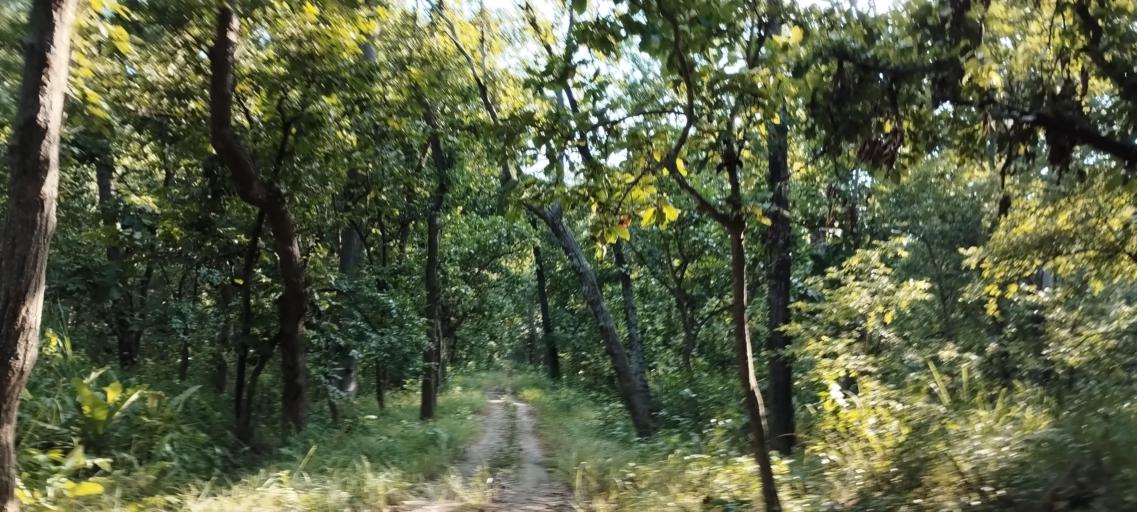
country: NP
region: Far Western
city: Tikapur
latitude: 28.5178
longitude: 81.2748
